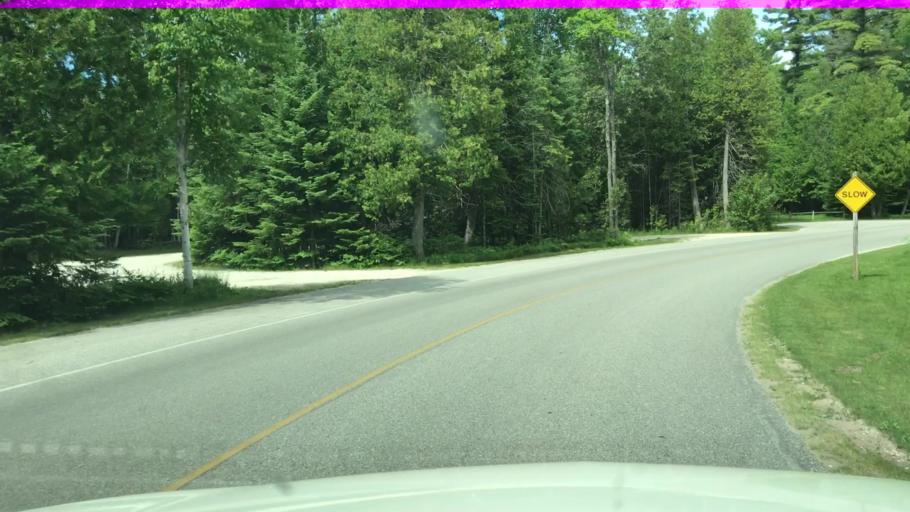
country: US
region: Michigan
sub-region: Schoolcraft County
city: Manistique
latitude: 45.9422
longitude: -86.3339
